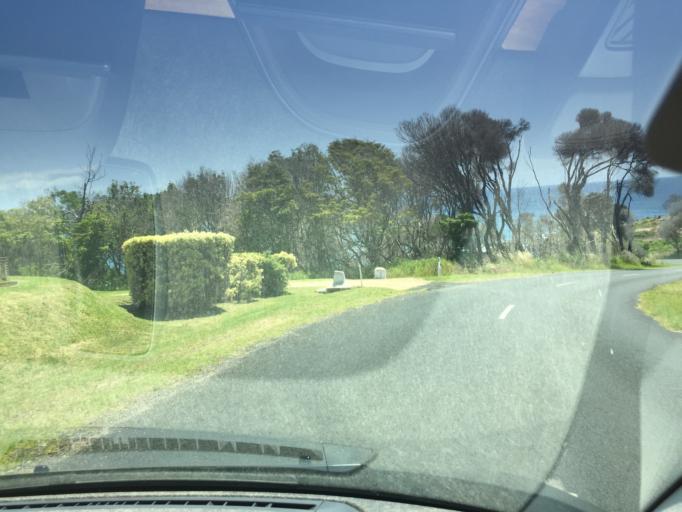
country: AU
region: New South Wales
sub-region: Bega Valley
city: Bega
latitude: -36.7276
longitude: 149.9872
